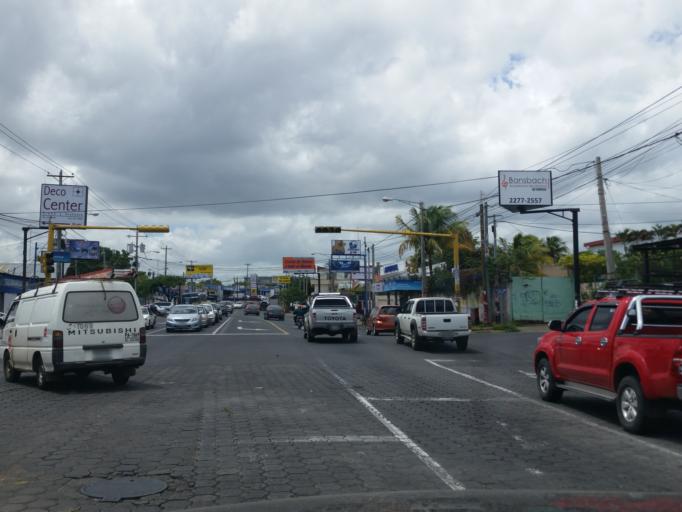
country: NI
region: Managua
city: Managua
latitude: 12.1258
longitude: -86.2549
